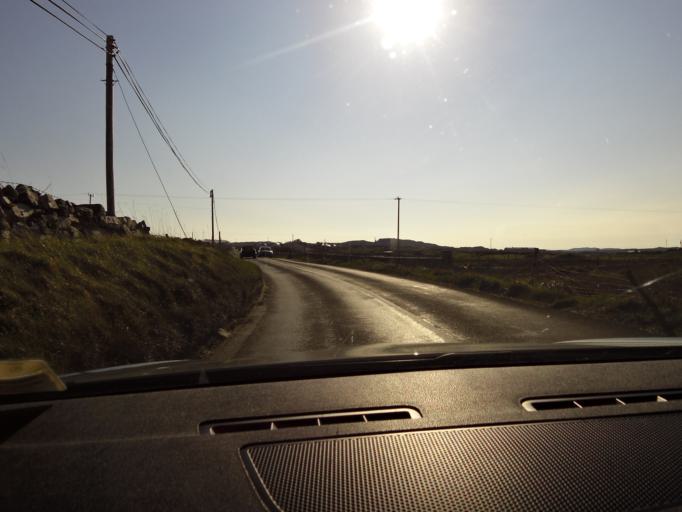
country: IE
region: Connaught
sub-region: County Galway
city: Clifden
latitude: 53.4403
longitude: -10.0657
